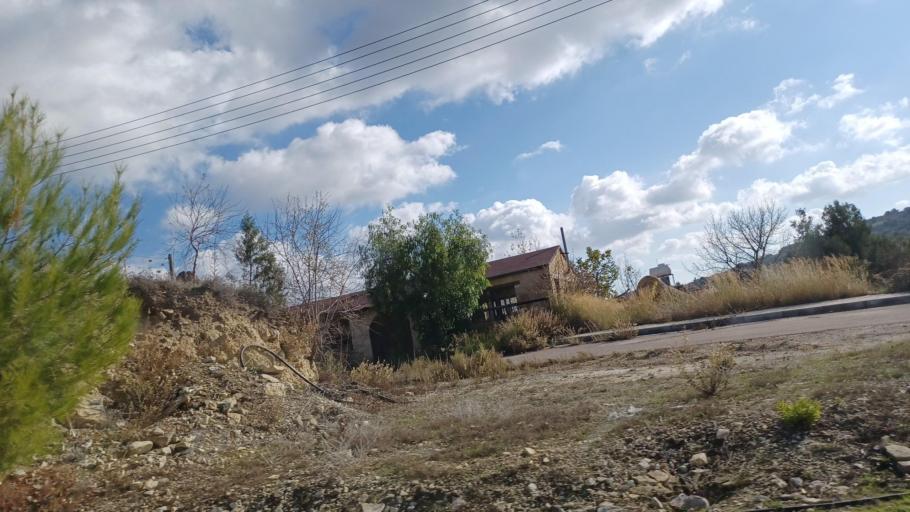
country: CY
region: Limassol
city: Pachna
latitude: 34.8356
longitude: 32.6871
